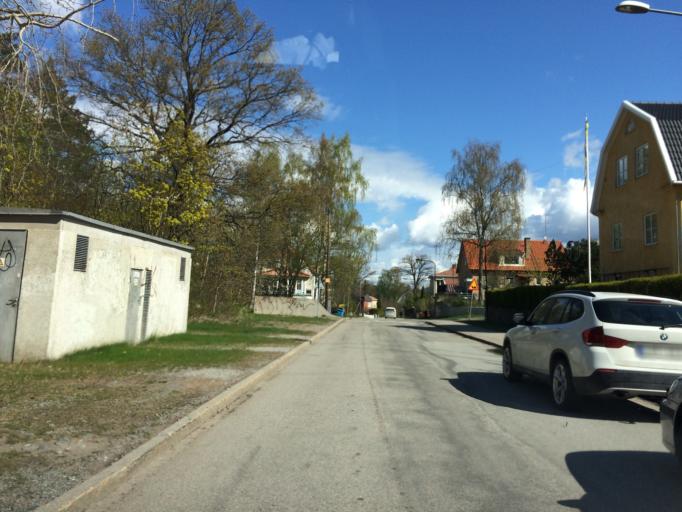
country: SE
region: Stockholm
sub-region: Huddinge Kommun
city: Segeltorp
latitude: 59.2977
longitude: 17.9485
